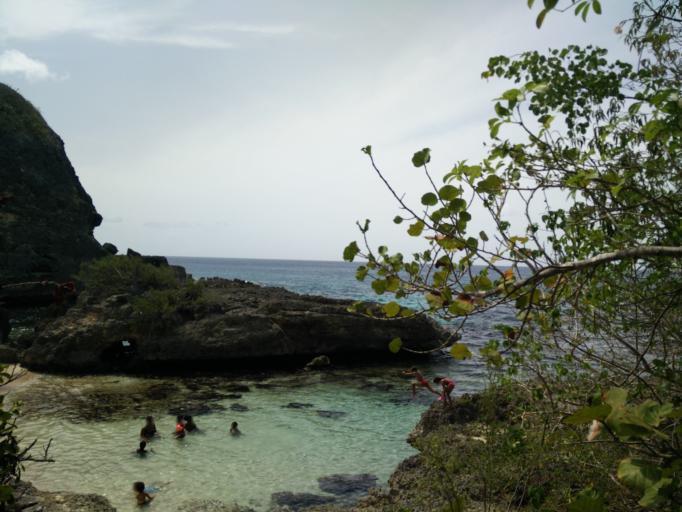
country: GP
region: Guadeloupe
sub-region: Guadeloupe
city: Anse-Bertrand
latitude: 16.4856
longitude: -61.4971
